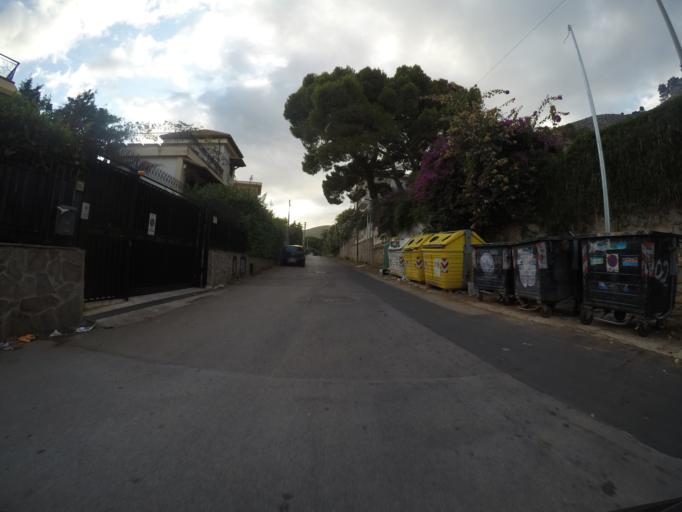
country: IT
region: Sicily
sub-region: Palermo
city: Isola delle Femmine
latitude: 38.2073
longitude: 13.3211
